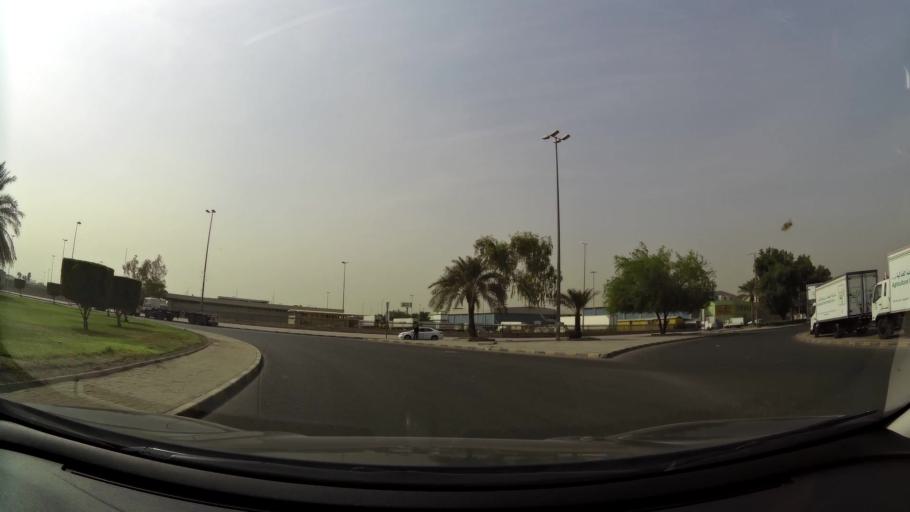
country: KW
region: Al Asimah
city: Ar Rabiyah
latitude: 29.3268
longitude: 47.9277
